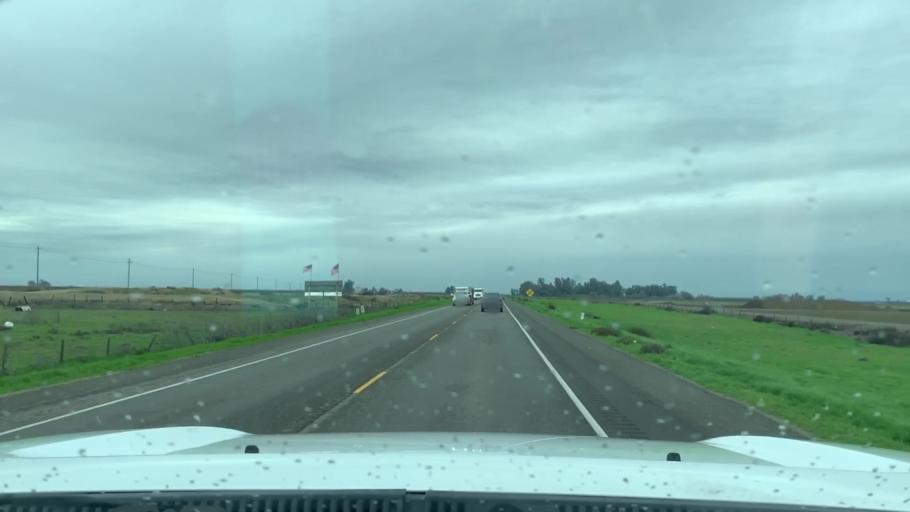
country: US
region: California
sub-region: Fresno County
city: Riverdale
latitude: 36.4501
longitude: -119.7974
